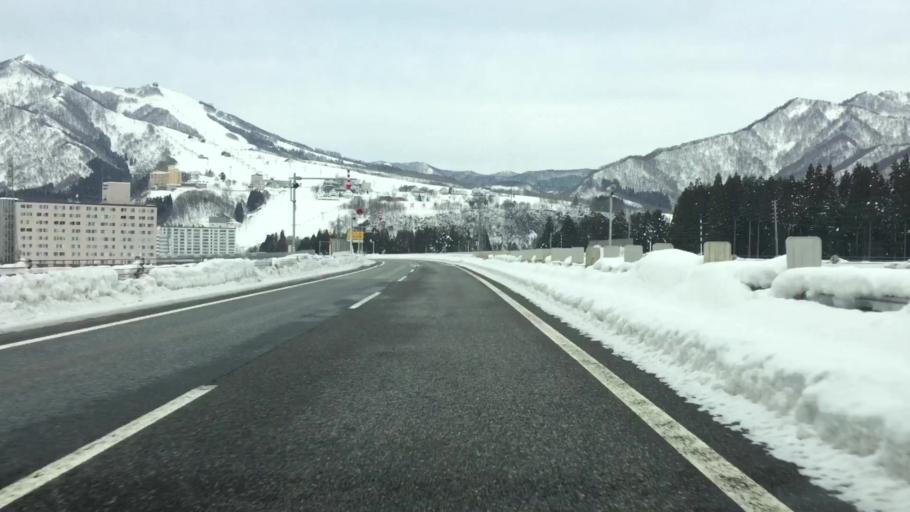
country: JP
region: Niigata
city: Shiozawa
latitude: 36.9214
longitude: 138.8411
